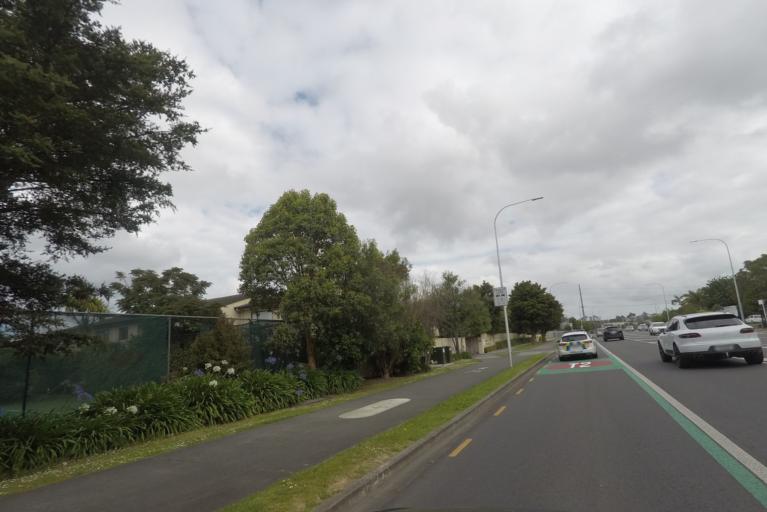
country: NZ
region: Auckland
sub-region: Auckland
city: Rothesay Bay
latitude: -36.7375
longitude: 174.6920
